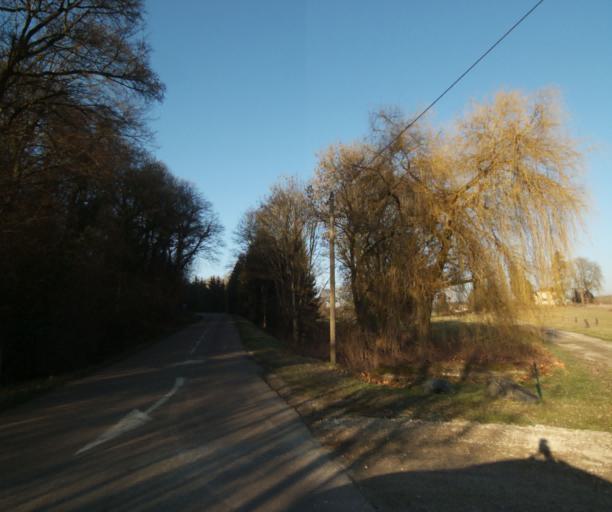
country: FR
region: Champagne-Ardenne
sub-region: Departement de la Haute-Marne
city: Bienville
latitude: 48.5557
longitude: 5.0870
